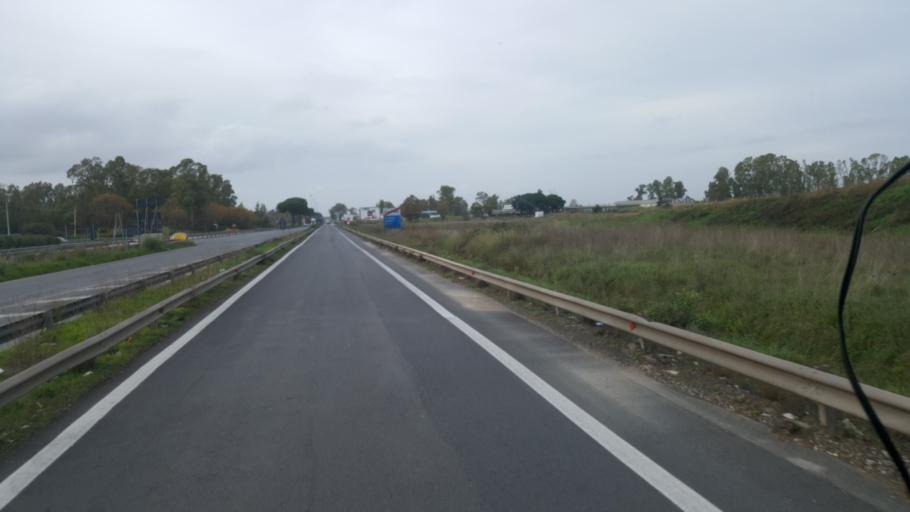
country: IT
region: Latium
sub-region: Provincia di Latina
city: Borgo Podgora
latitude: 41.4839
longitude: 12.8587
